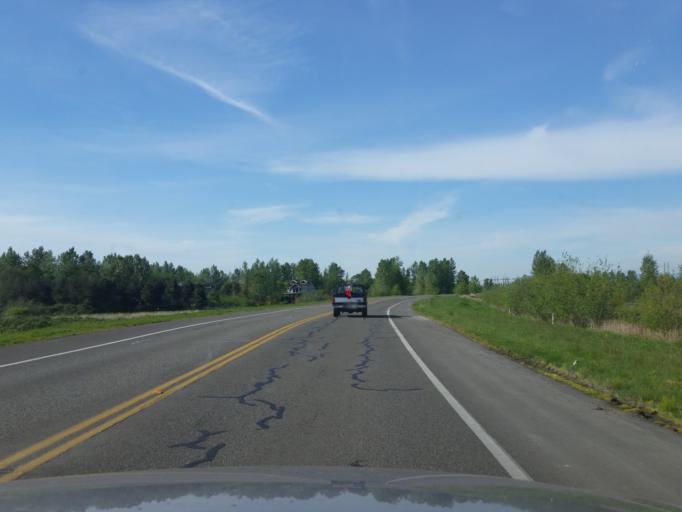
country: US
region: Washington
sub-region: Snohomish County
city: Fobes Hill
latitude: 47.9311
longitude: -122.1719
